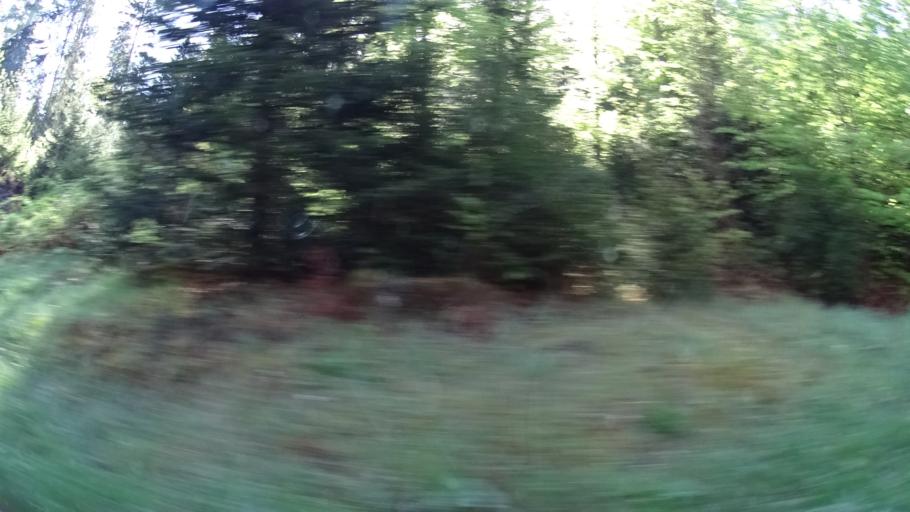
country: DE
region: Baden-Wuerttemberg
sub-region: Karlsruhe Region
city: Bad Wildbad
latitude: 48.7245
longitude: 8.5676
